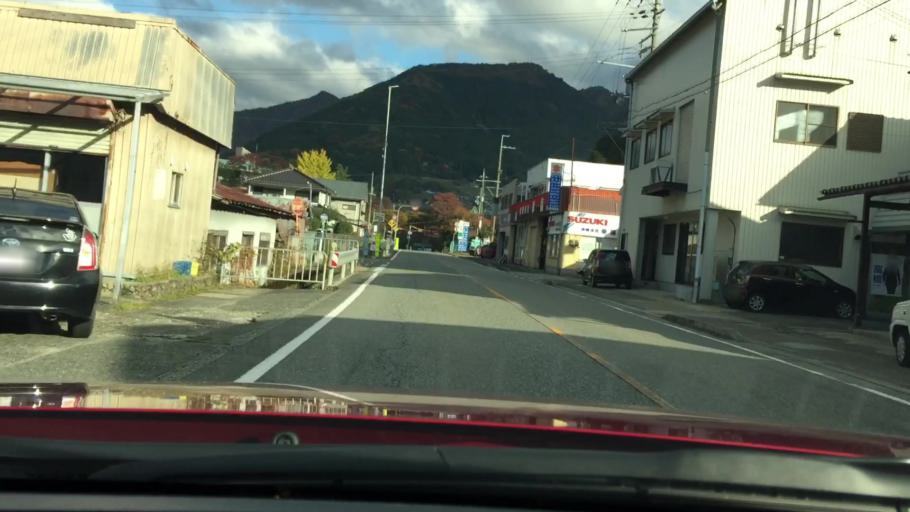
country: JP
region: Hyogo
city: Yamazakicho-nakabirose
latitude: 35.1675
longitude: 134.5444
